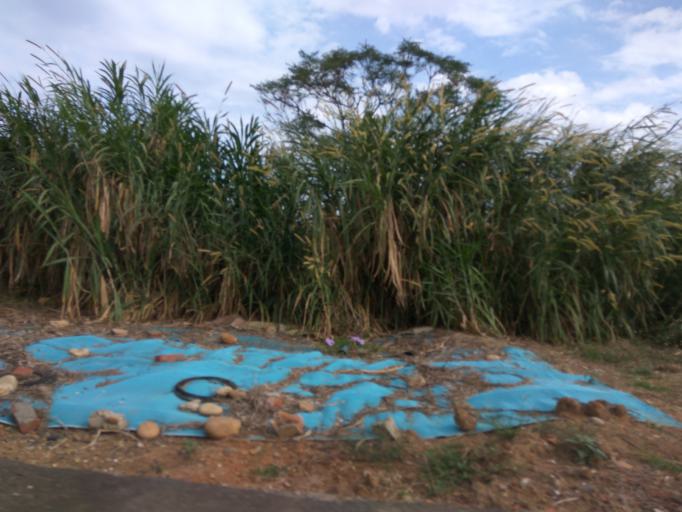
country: TW
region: Taiwan
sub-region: Hsinchu
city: Zhubei
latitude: 24.9501
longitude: 121.0015
